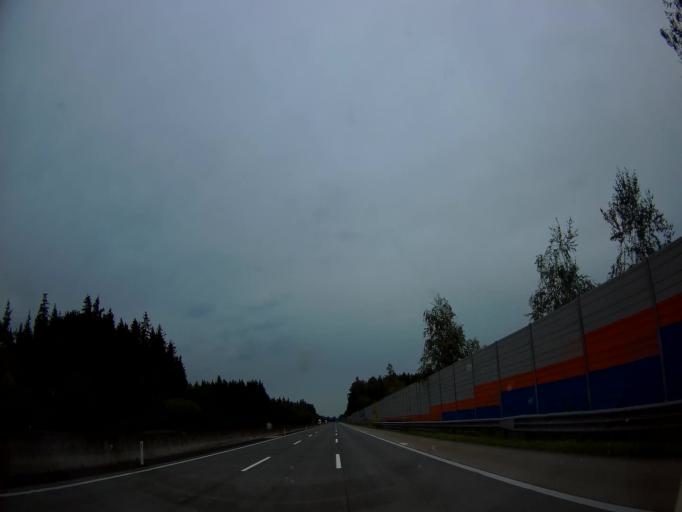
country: AT
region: Upper Austria
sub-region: Politischer Bezirk Kirchdorf an der Krems
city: Kremsmunster
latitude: 48.1158
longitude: 14.1041
